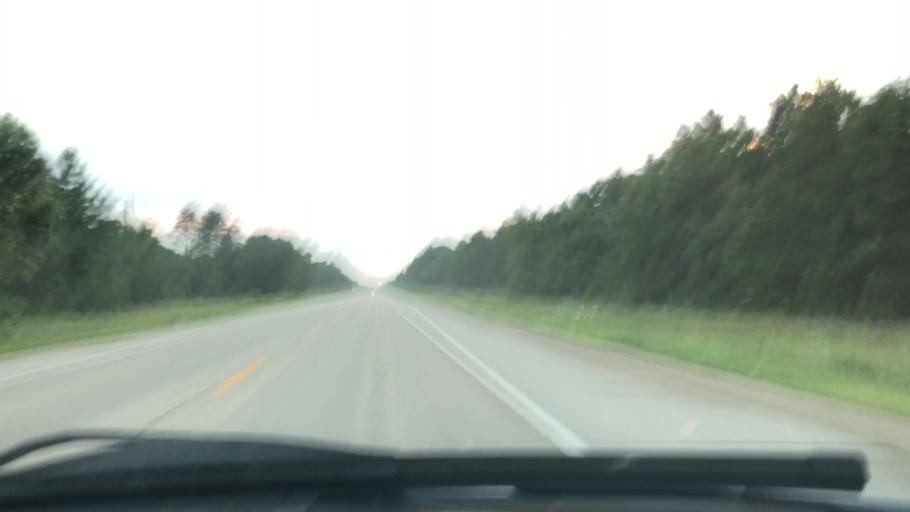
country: US
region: Wisconsin
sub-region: Sauk County
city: Spring Green
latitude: 43.1912
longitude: -90.1816
